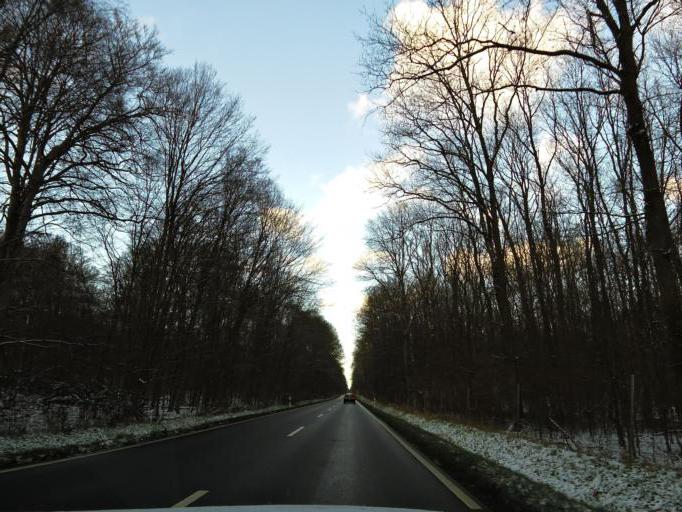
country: DE
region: Hesse
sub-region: Regierungsbezirk Darmstadt
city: Messel
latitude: 49.9223
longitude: 8.7209
